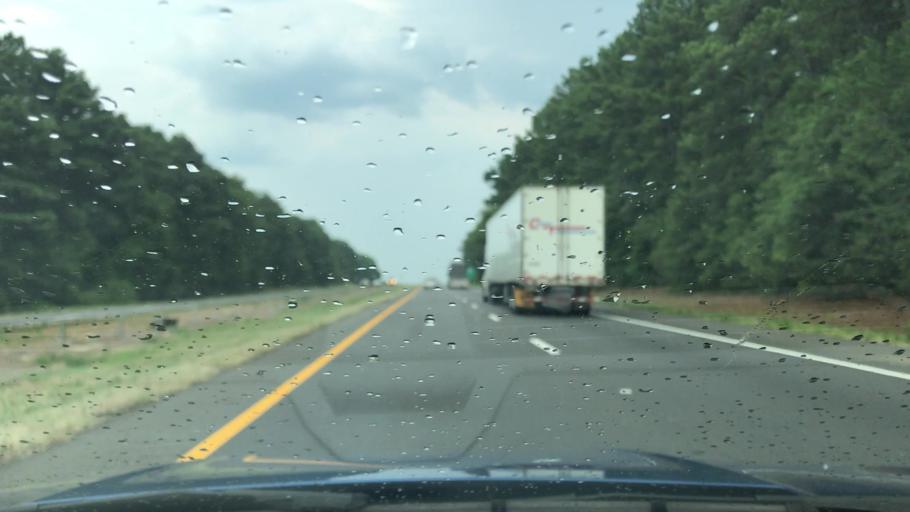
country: US
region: Texas
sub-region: Harrison County
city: Marshall
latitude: 32.4885
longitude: -94.4202
